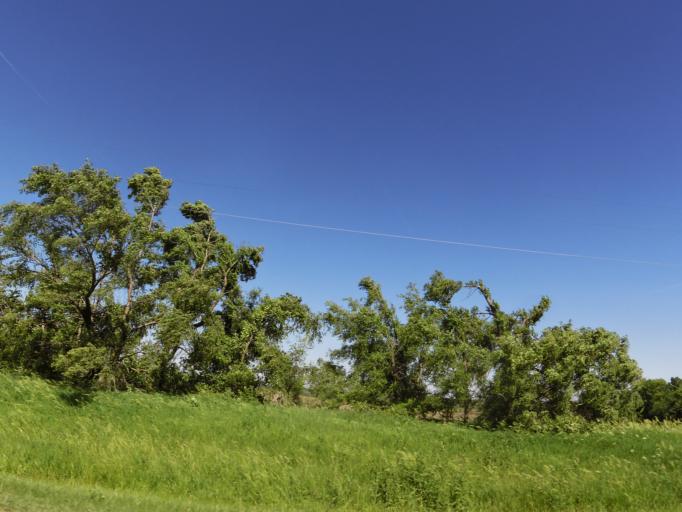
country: US
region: Illinois
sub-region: Ogle County
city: Davis Junction
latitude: 42.1407
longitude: -89.0769
